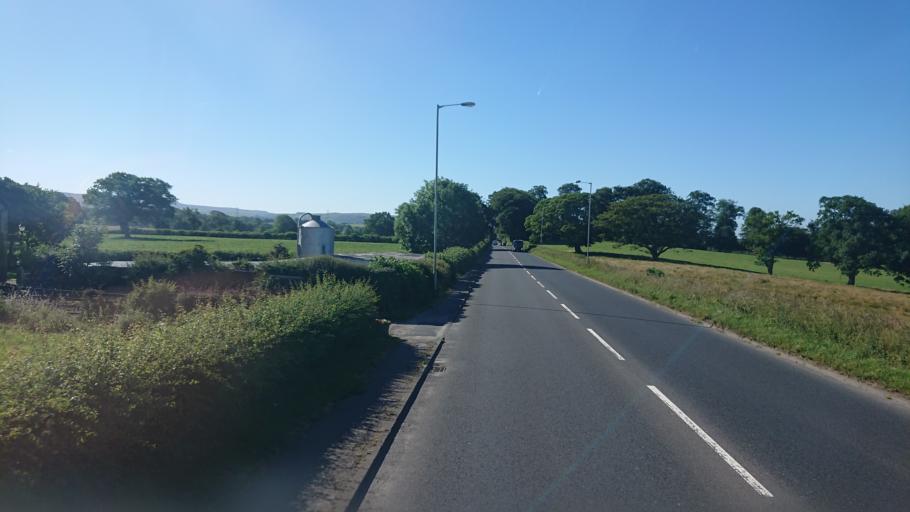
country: GB
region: England
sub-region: Lancashire
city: Bay Horse
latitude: 53.9735
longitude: -2.7841
